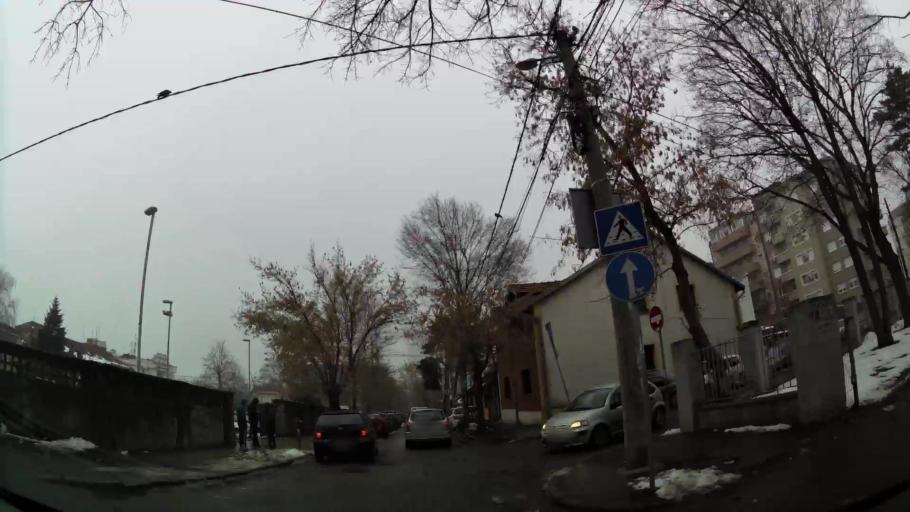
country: RS
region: Central Serbia
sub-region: Belgrade
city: Vozdovac
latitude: 44.7740
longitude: 20.4750
